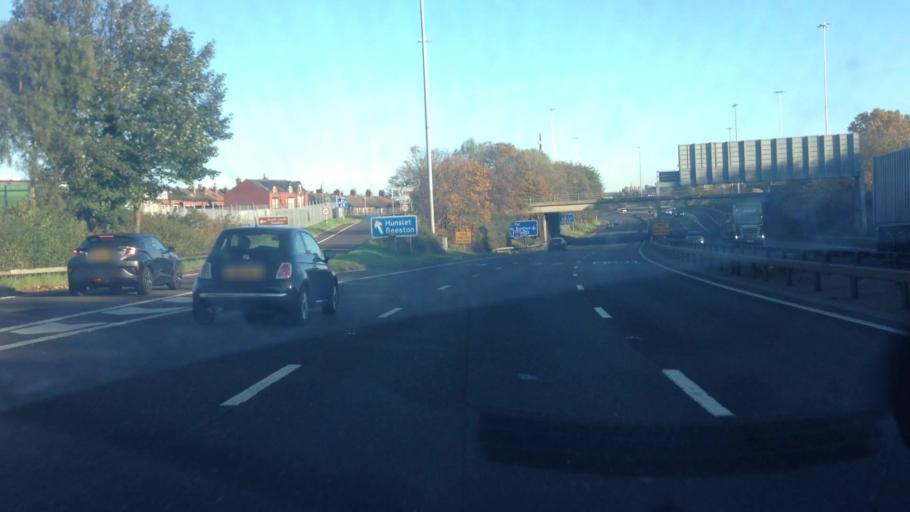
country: GB
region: England
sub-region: City and Borough of Leeds
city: Leeds
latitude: 53.7746
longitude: -1.5401
